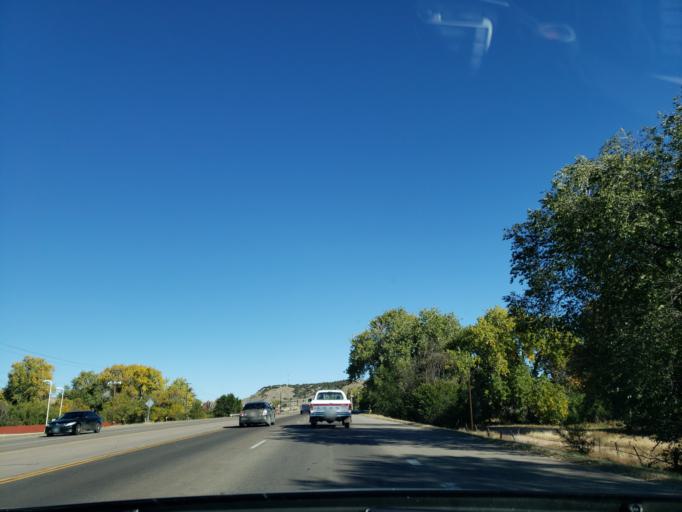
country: US
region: Colorado
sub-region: Fremont County
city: Lincoln Park
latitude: 38.4470
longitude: -105.1868
